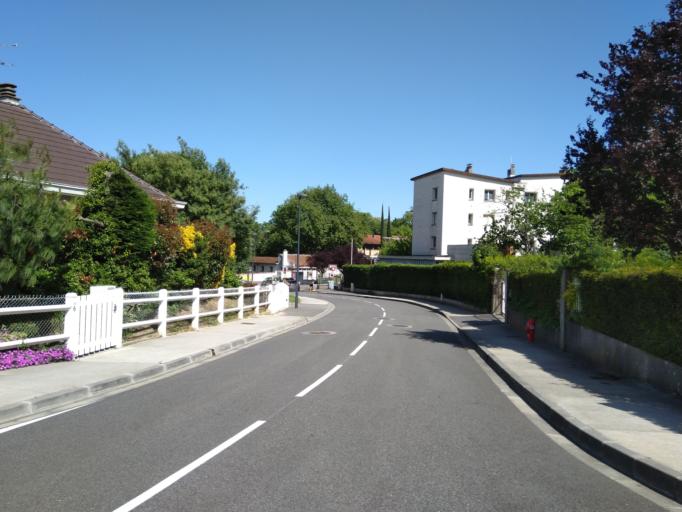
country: FR
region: Midi-Pyrenees
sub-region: Departement de la Haute-Garonne
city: Ramonville-Saint-Agne
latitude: 43.5482
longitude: 1.4708
